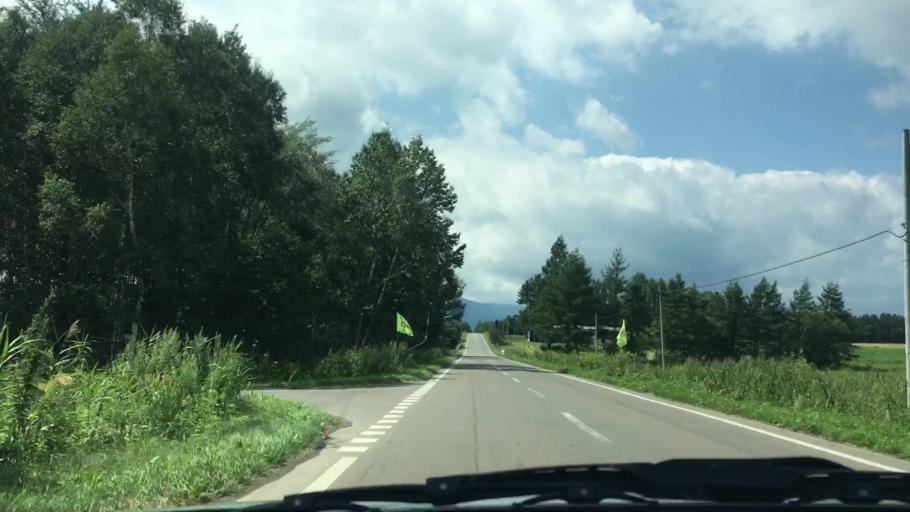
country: JP
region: Hokkaido
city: Otofuke
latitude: 43.2769
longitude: 143.3676
